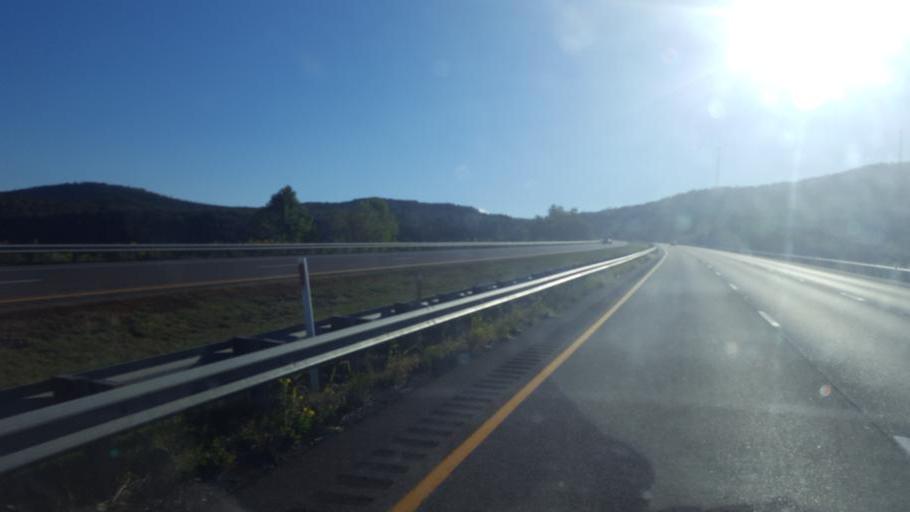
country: US
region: Maryland
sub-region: Allegany County
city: Cumberland
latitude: 39.6953
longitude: -78.5438
